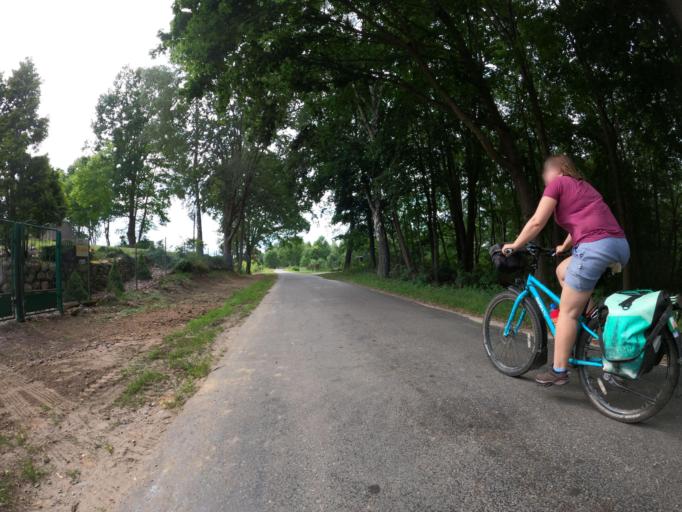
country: PL
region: West Pomeranian Voivodeship
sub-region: Powiat szczecinecki
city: Borne Sulinowo
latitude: 53.6291
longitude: 16.5578
